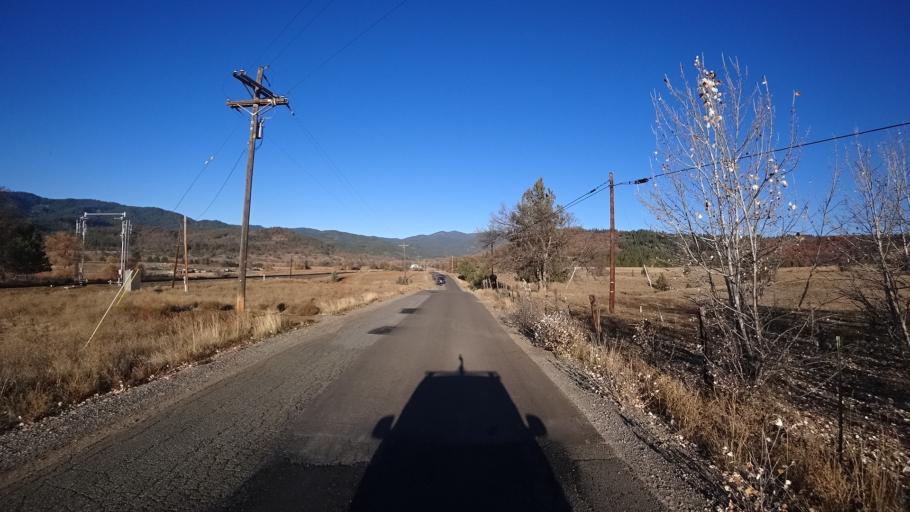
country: US
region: Oregon
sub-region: Jackson County
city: Ashland
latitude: 41.9967
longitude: -122.6272
